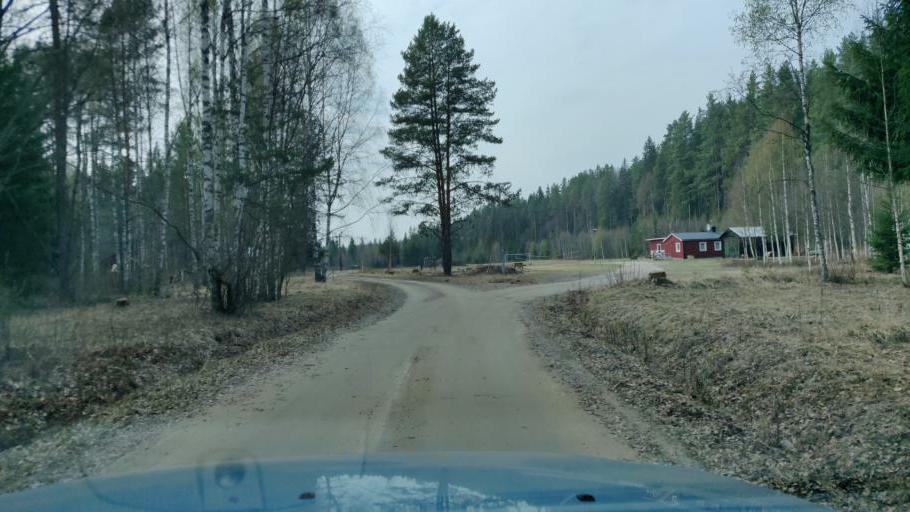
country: SE
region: Vaermland
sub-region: Munkfors Kommun
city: Munkfors
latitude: 59.8744
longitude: 13.5485
